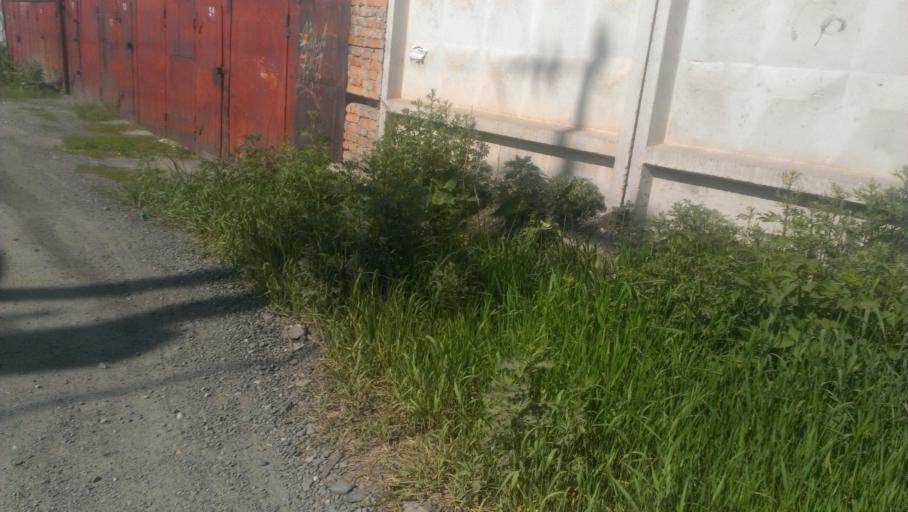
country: RU
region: Altai Krai
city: Novoaltaysk
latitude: 53.3980
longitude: 83.9383
